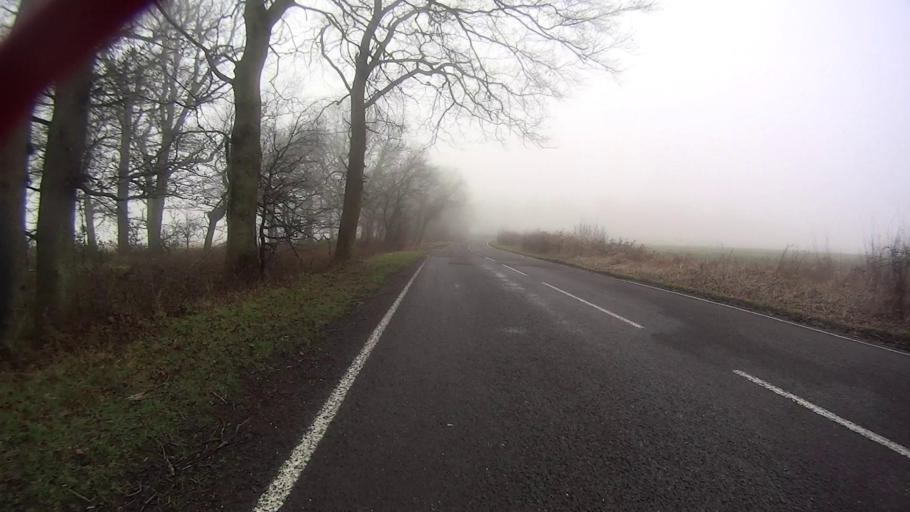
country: GB
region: England
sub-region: Surrey
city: Newdigate
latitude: 51.1408
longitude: -0.3176
